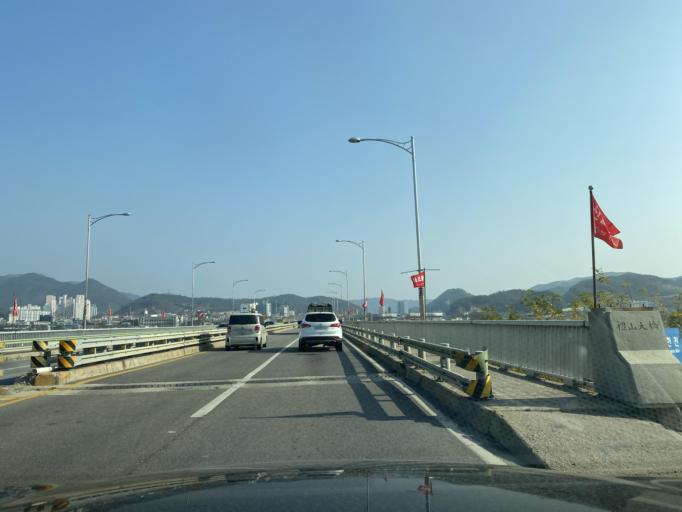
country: KR
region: Chungcheongnam-do
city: Yesan
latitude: 36.6844
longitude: 126.8191
